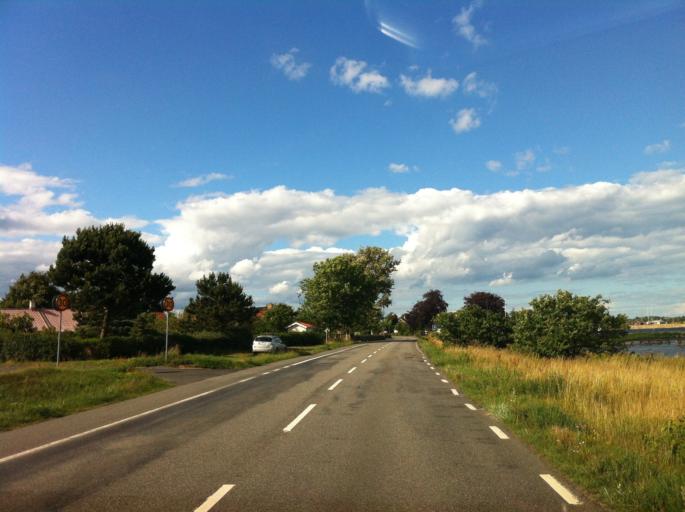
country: SE
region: Skane
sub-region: Simrishamns Kommun
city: Simrishamn
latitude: 55.4635
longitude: 14.2769
